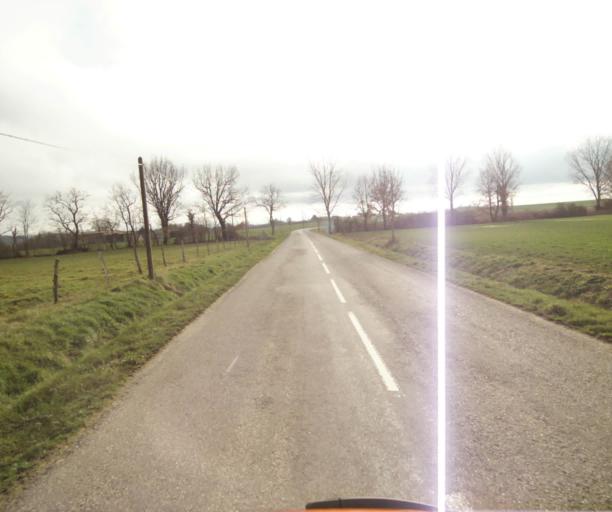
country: FR
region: Languedoc-Roussillon
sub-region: Departement de l'Aude
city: Belpech
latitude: 43.1935
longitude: 1.7293
